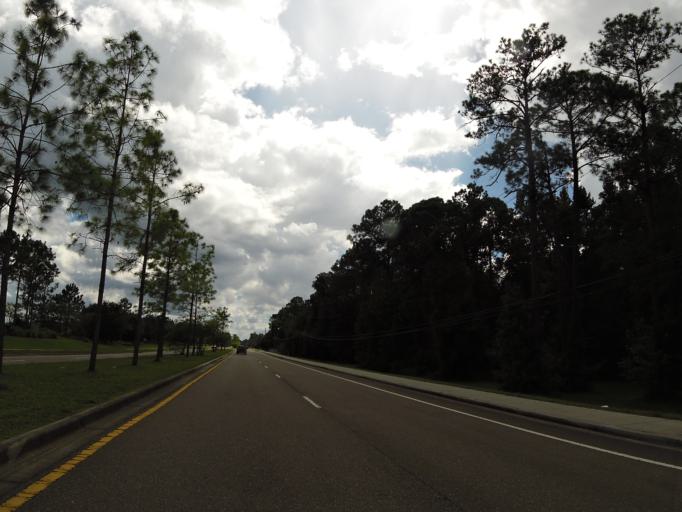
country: US
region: Florida
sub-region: Clay County
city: Green Cove Springs
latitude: 29.9572
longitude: -81.4944
